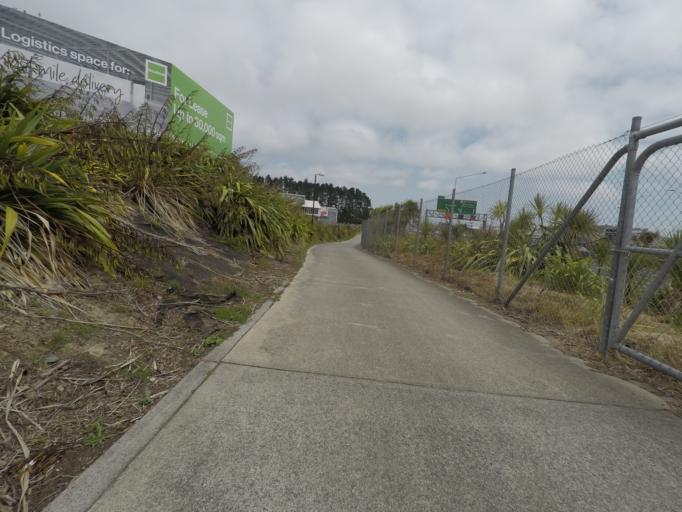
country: NZ
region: Auckland
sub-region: Auckland
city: Auckland
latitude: -36.9080
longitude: 174.7308
